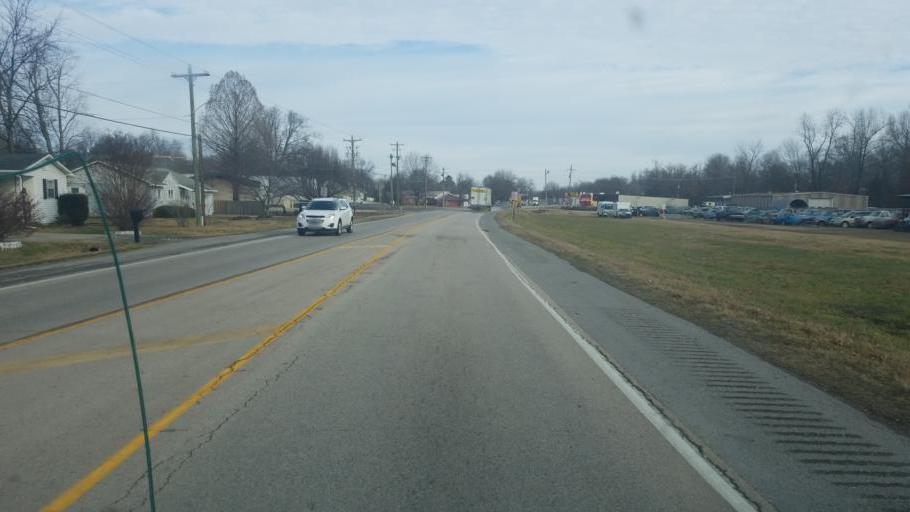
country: US
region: Missouri
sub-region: Stoddard County
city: Bloomfield
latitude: 36.8796
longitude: -89.9267
